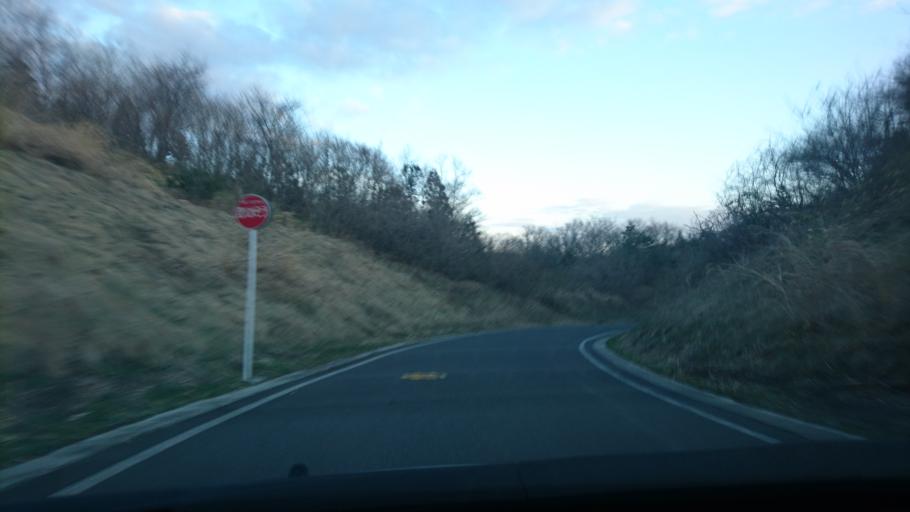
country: JP
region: Iwate
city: Ichinoseki
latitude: 38.9023
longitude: 141.1686
